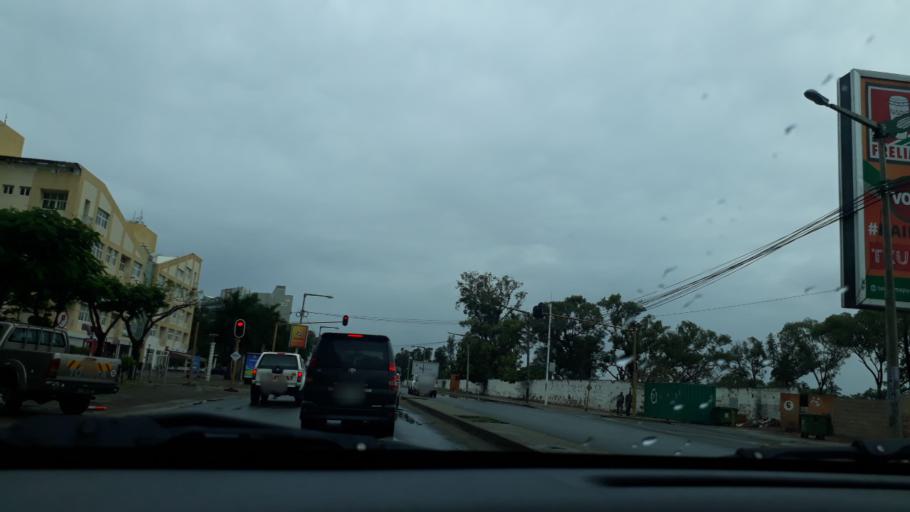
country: MZ
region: Maputo City
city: Maputo
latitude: -25.9780
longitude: 32.5802
